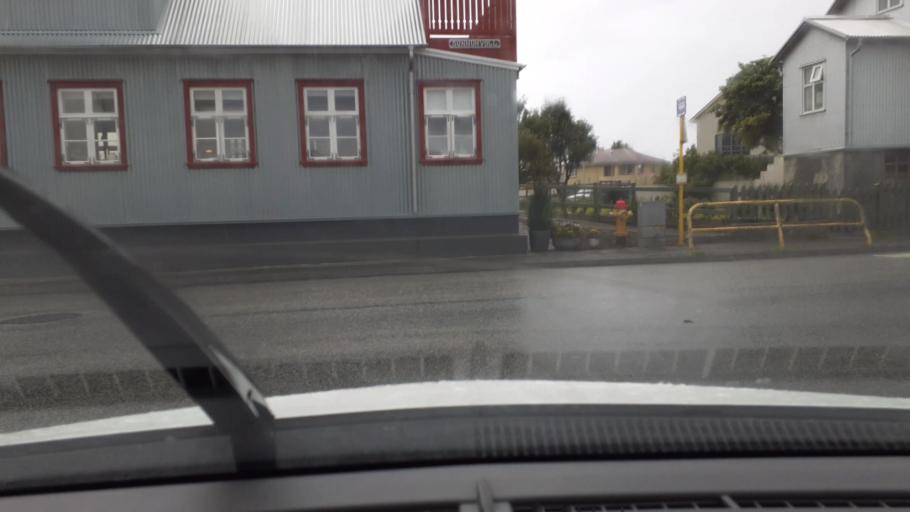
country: IS
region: West
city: Akranes
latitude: 64.3171
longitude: -22.0841
